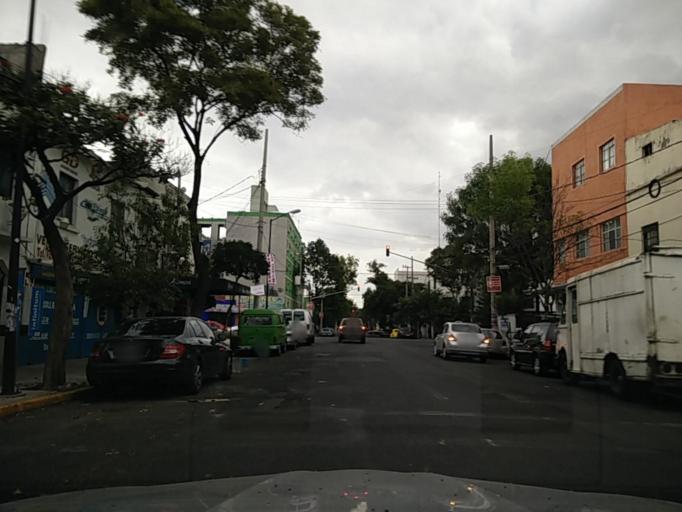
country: MX
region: Mexico City
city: Mexico City
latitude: 19.4101
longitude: -99.1392
